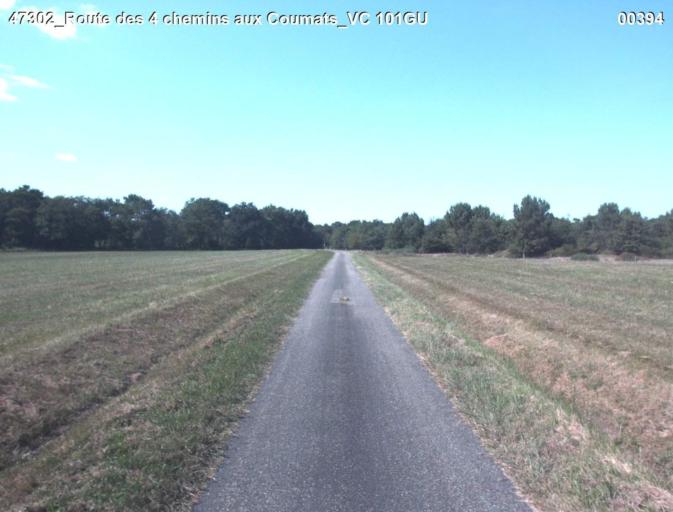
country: FR
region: Aquitaine
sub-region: Departement des Landes
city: Gabarret
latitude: 44.0188
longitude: 0.0866
